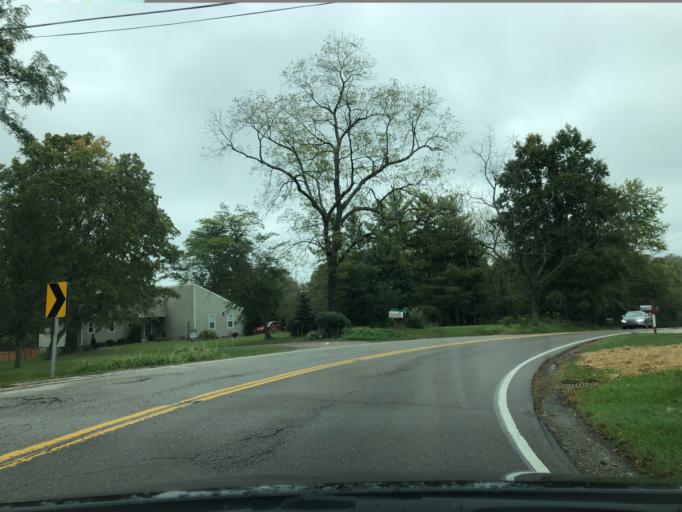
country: US
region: Ohio
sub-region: Hamilton County
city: Loveland
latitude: 39.2402
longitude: -84.2621
